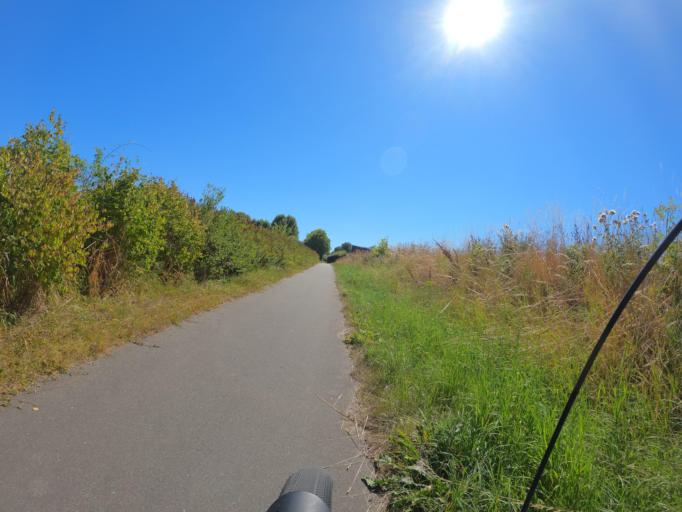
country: DE
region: Schleswig-Holstein
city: Quern
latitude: 54.7846
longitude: 9.7258
